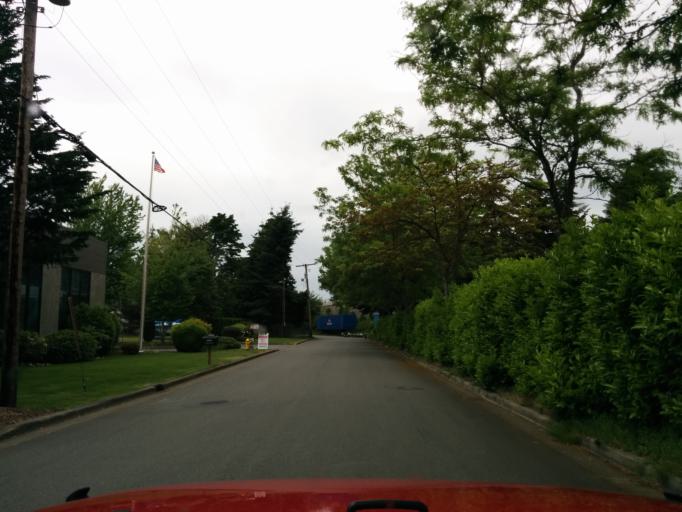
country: US
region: Washington
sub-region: King County
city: Redmond
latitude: 47.6676
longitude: -122.1079
